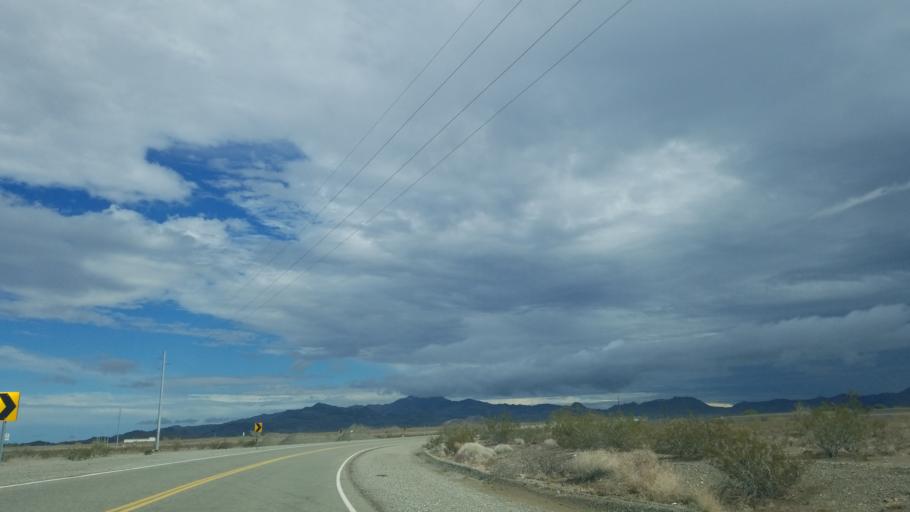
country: US
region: Arizona
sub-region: La Paz County
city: Salome
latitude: 33.7316
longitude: -113.7656
